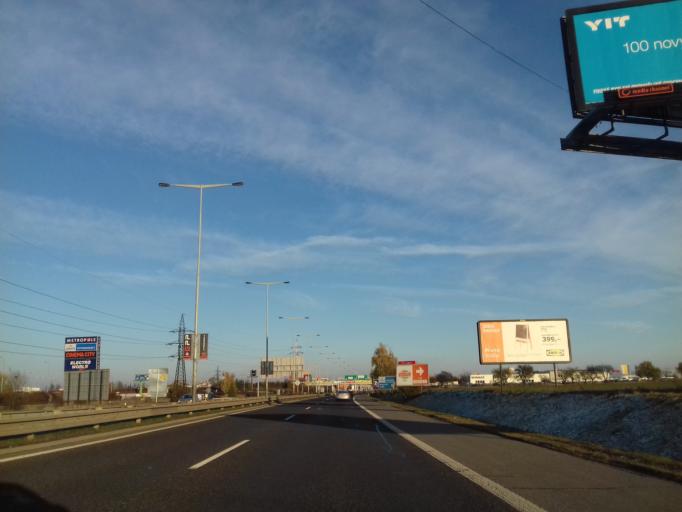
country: CZ
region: Central Bohemia
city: Hostivice
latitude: 50.0507
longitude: 14.2860
